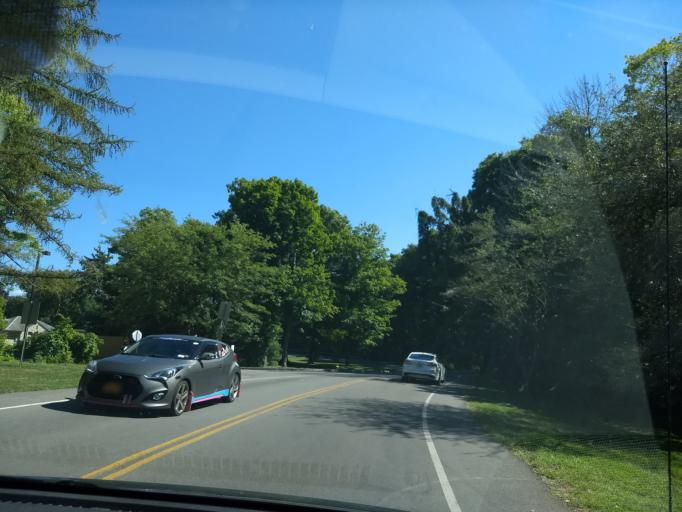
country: US
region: New York
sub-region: Niagara County
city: Niagara Falls
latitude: 43.0811
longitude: -79.0664
